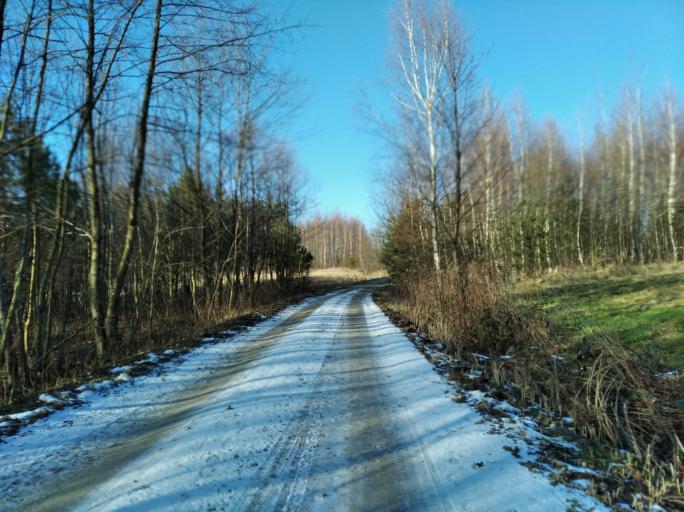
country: PL
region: Subcarpathian Voivodeship
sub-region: Powiat strzyzowski
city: Jawornik
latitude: 49.8355
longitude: 21.8581
